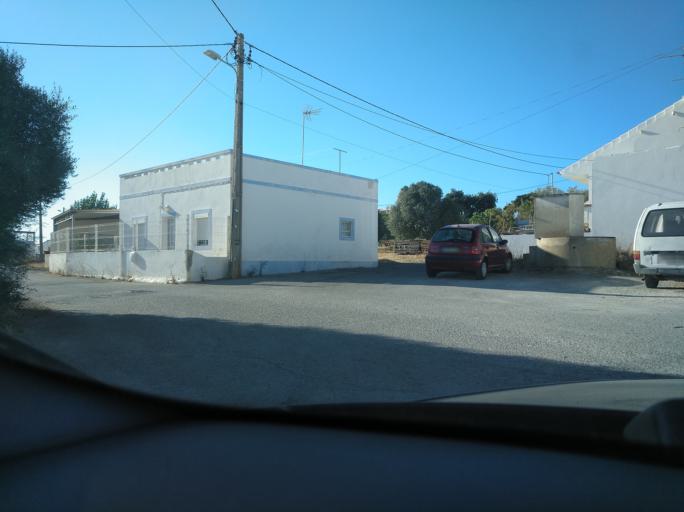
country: PT
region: Faro
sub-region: Vila Real de Santo Antonio
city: Monte Gordo
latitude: 37.1835
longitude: -7.5110
